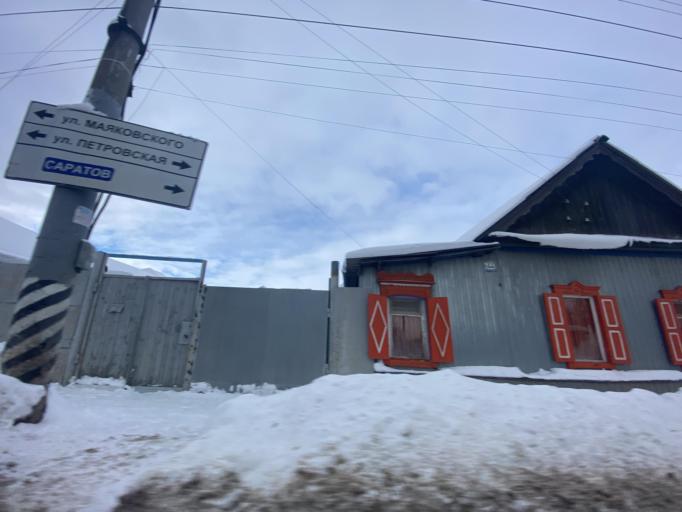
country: RU
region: Saratov
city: Engel's
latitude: 51.5018
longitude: 46.1101
